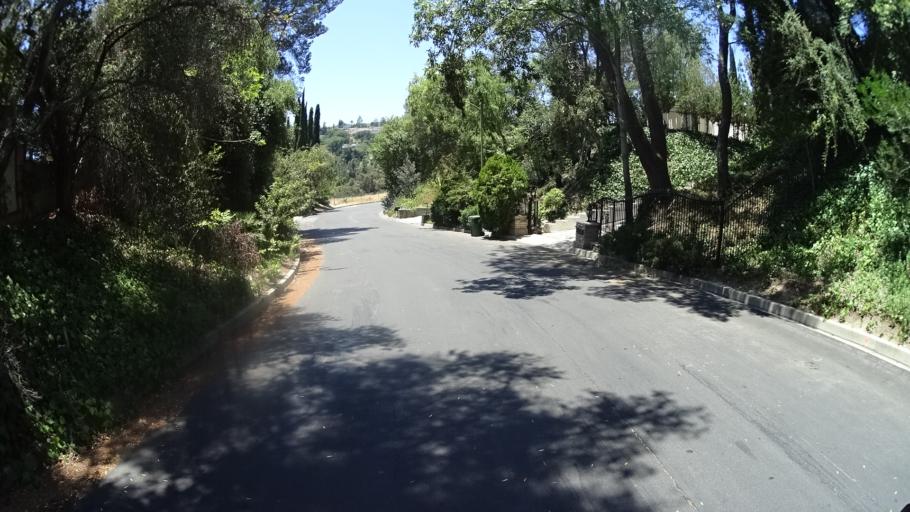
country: US
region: California
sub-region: Los Angeles County
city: Sherman Oaks
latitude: 34.1451
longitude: -118.4778
